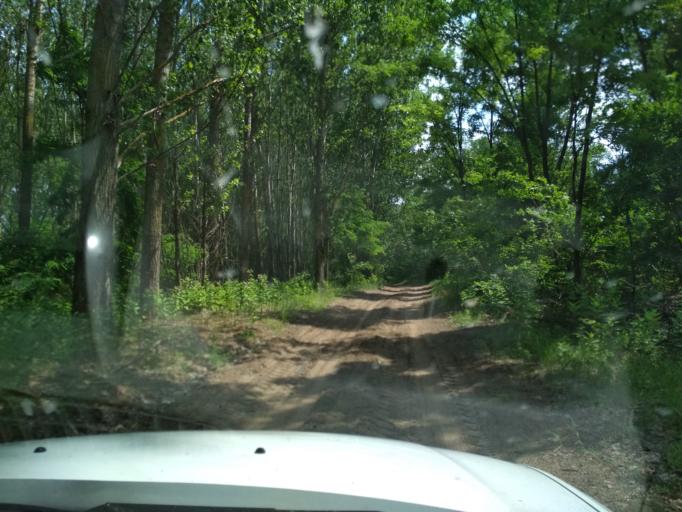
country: HU
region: Pest
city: Tapioszentmarton
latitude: 47.3602
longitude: 19.7437
